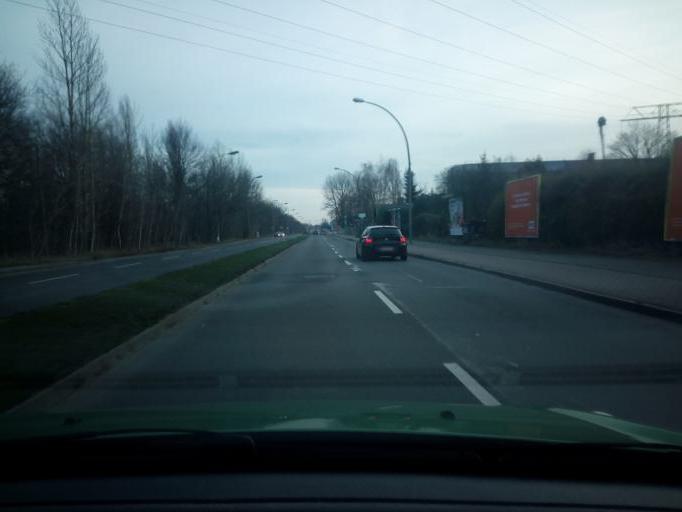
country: DE
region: Berlin
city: Oberschoneweide
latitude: 52.4761
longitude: 13.5064
